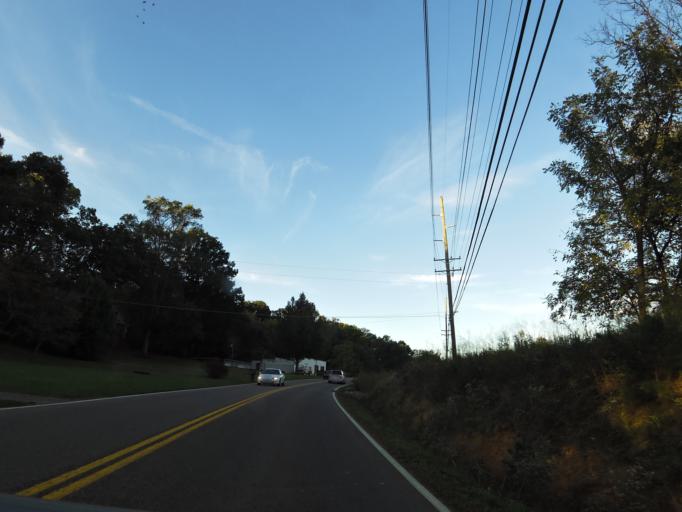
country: US
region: Tennessee
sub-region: Sevier County
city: Pigeon Forge
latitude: 35.7163
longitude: -83.6515
